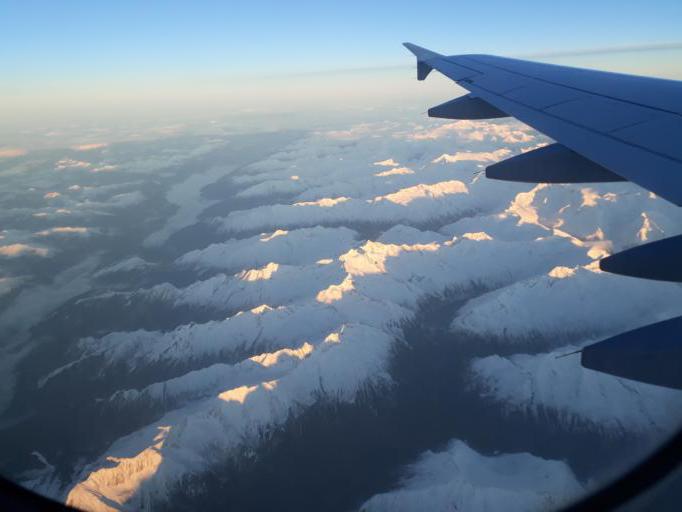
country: AT
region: Tyrol
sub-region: Politischer Bezirk Schwaz
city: Mayrhofen
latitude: 47.1265
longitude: 11.8791
